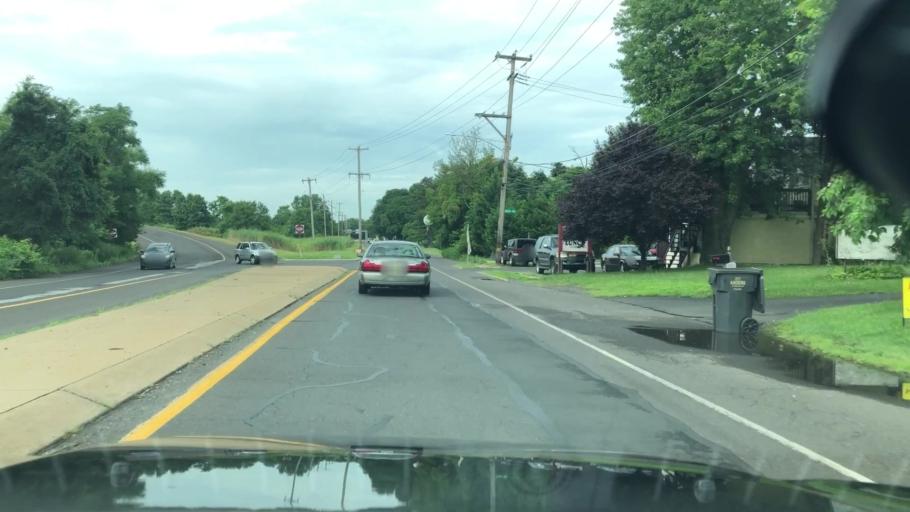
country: US
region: Pennsylvania
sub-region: Bucks County
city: Morrisville
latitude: 40.2013
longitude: -74.7878
